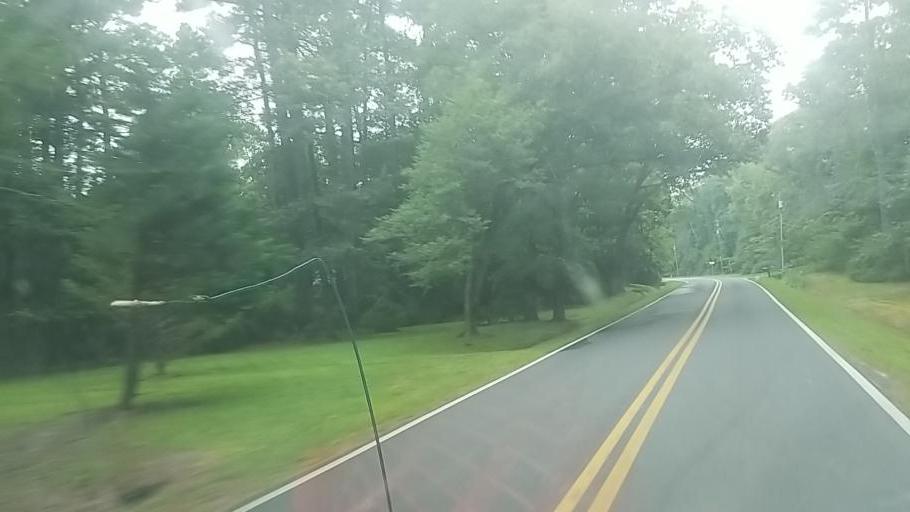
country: US
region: Maryland
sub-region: Wicomico County
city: Delmar
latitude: 38.4089
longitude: -75.5164
